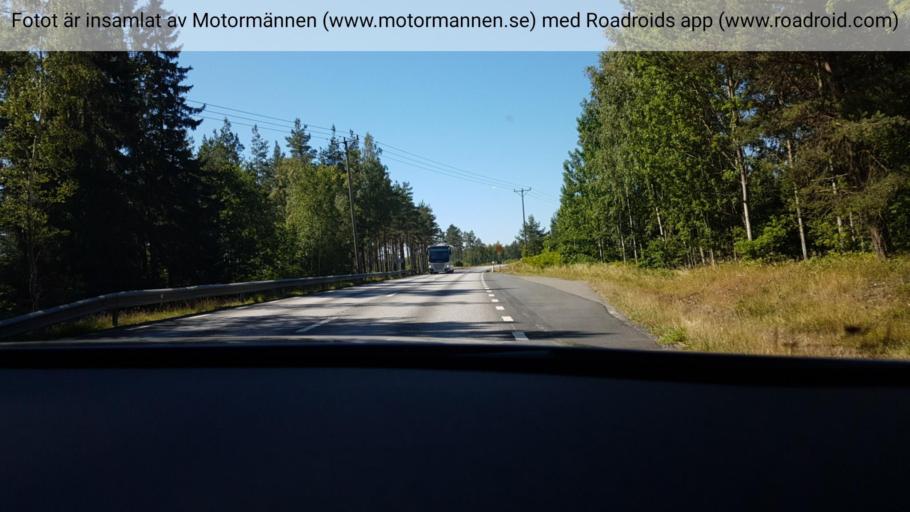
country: SE
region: Joenkoeping
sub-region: Habo Kommun
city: Habo
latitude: 58.0399
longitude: 14.1798
